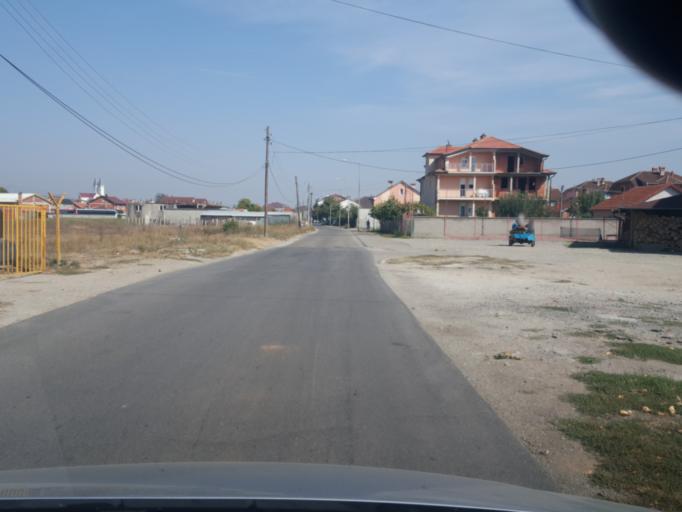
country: XK
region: Gjakova
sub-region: Komuna e Gjakoves
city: Gjakove
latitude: 42.3698
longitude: 20.4095
